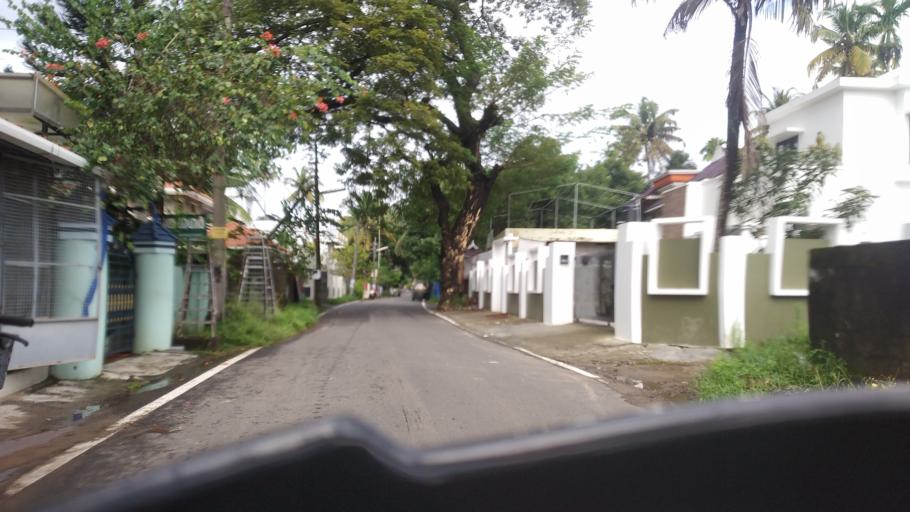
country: IN
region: Kerala
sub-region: Ernakulam
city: Elur
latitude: 10.1006
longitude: 76.1985
